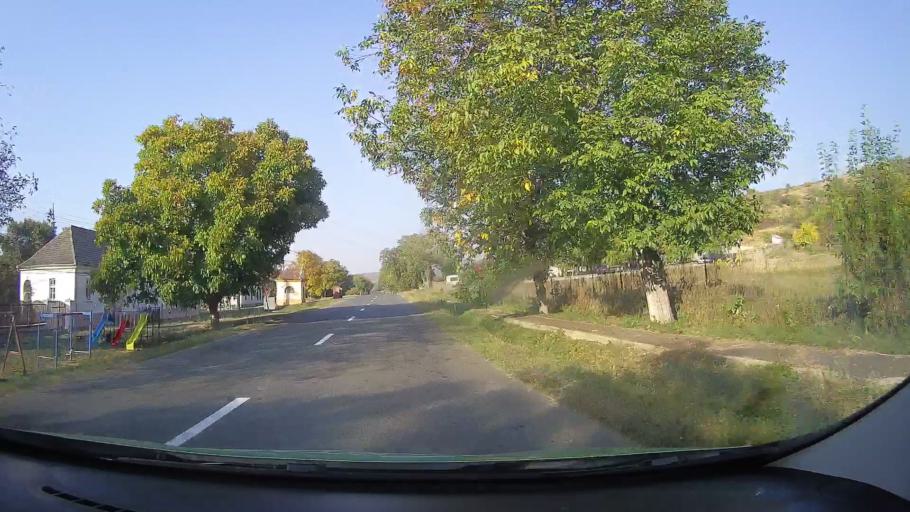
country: RO
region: Arad
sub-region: Comuna Paulis
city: Paulis
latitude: 46.1232
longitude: 21.5983
